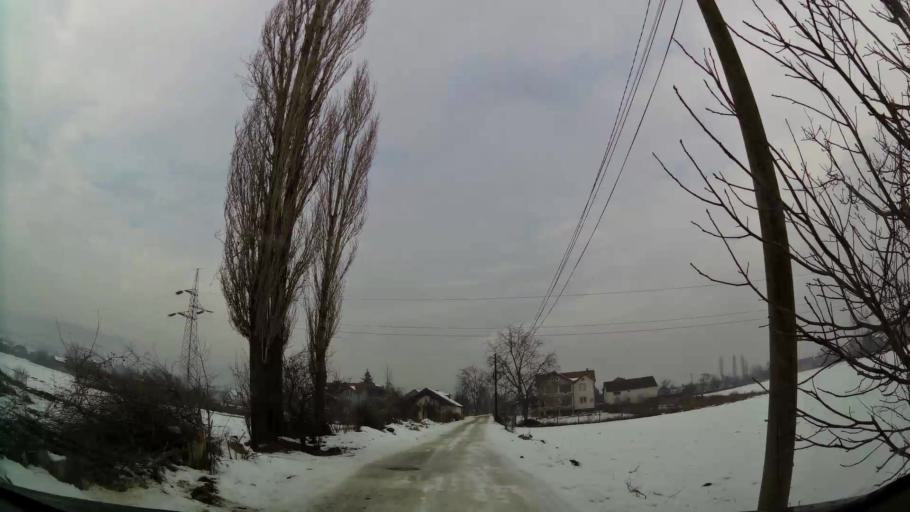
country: MK
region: Saraj
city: Saraj
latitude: 42.0423
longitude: 21.3570
